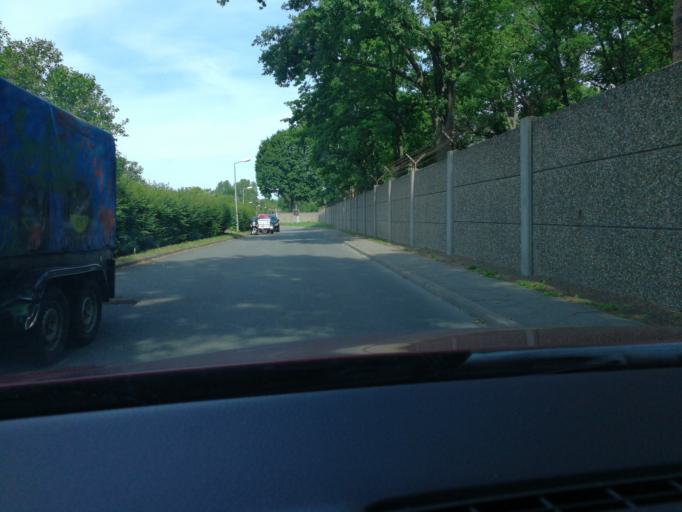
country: DE
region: Berlin
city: Reinickendorf
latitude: 52.5505
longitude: 13.3199
